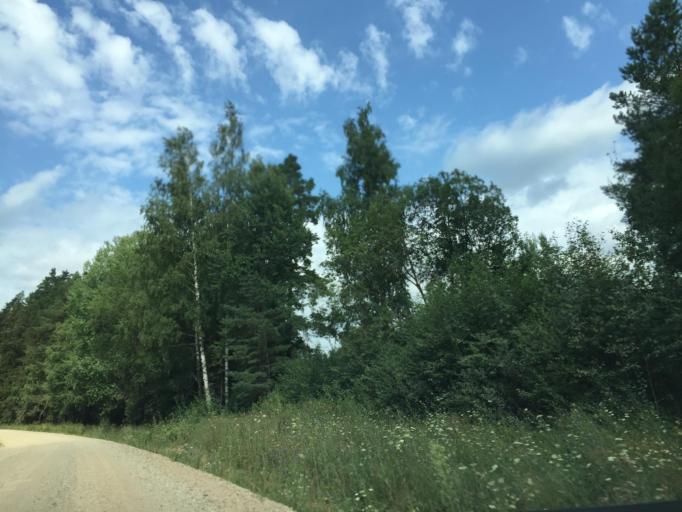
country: LV
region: Kandava
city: Kandava
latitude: 57.0076
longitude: 22.8434
